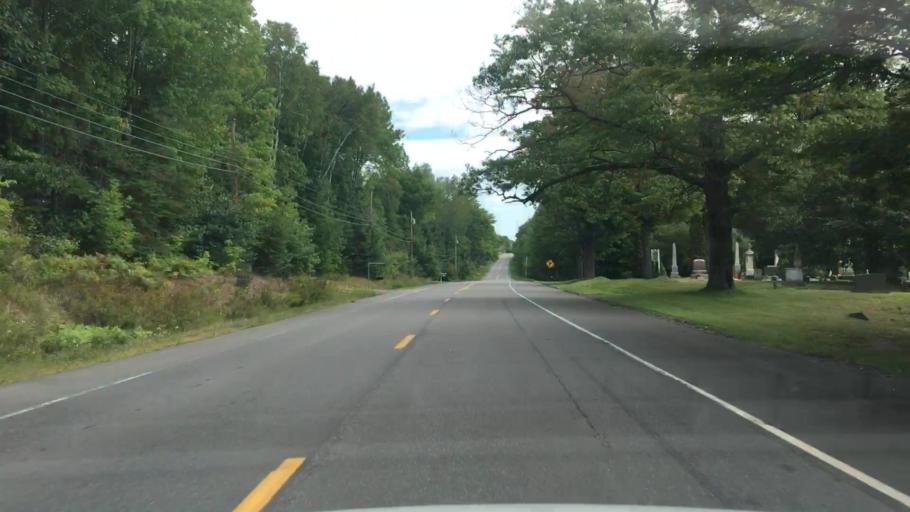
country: US
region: Maine
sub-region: Piscataquis County
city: Brownville
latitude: 45.2266
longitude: -69.1167
